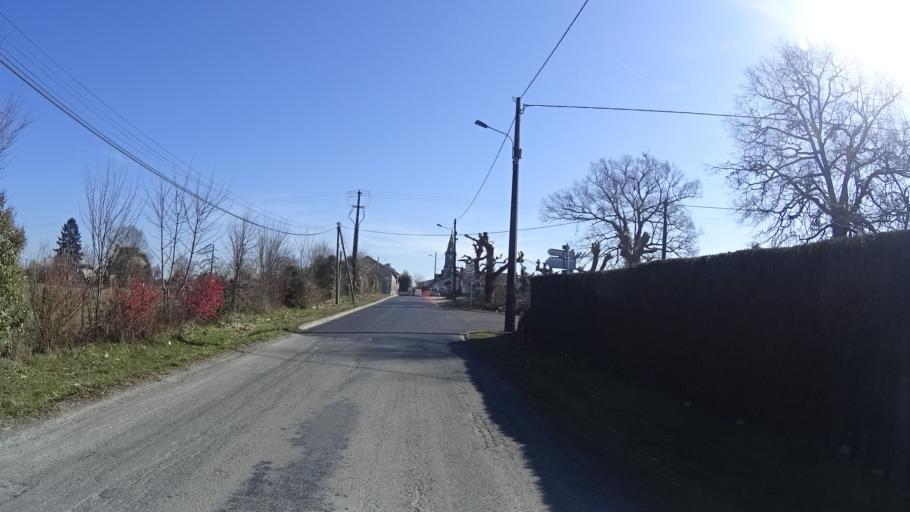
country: FR
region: Aquitaine
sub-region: Departement de la Dordogne
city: Saint-Aulaye
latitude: 45.1265
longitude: 0.2274
